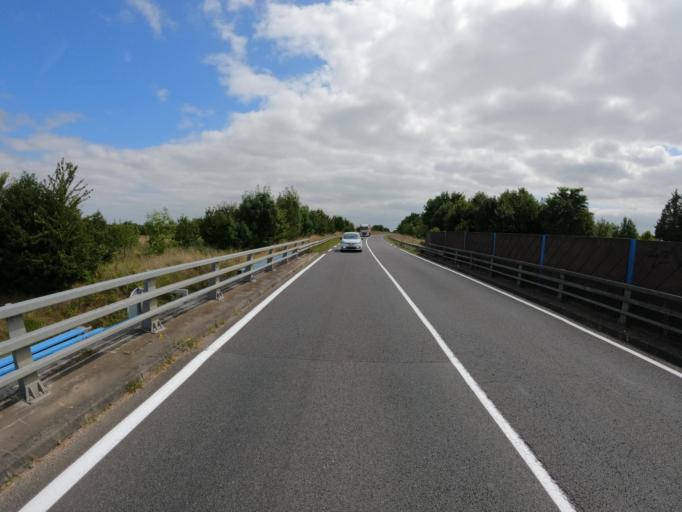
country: FR
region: Poitou-Charentes
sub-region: Departement de la Vienne
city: Charroux
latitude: 46.1530
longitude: 0.3988
